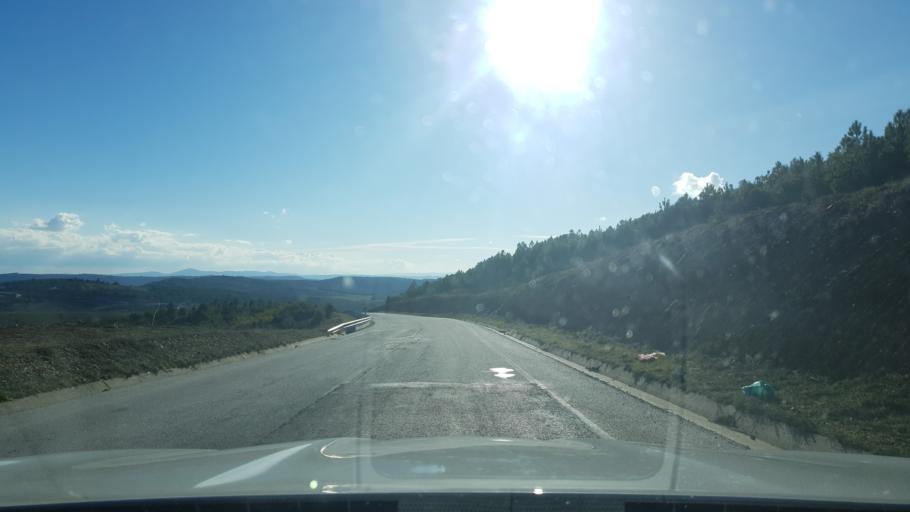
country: PT
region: Braganca
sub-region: Freixo de Espada A Cinta
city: Freixo de Espada a Cinta
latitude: 41.1329
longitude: -6.8130
